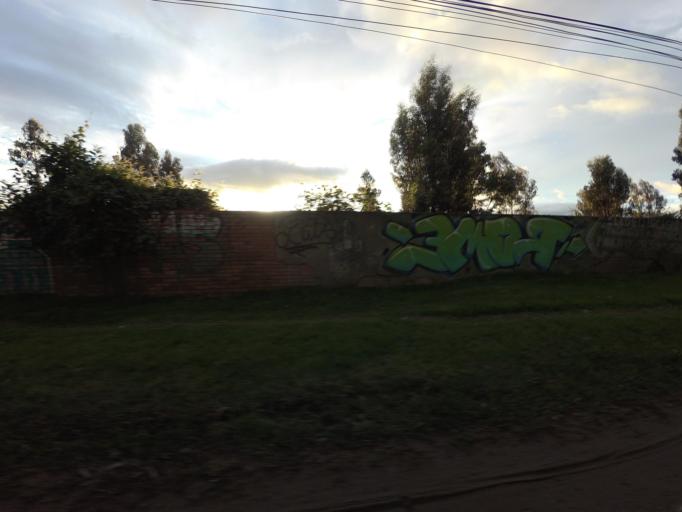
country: CO
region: Cundinamarca
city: La Calera
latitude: 4.7722
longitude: -74.0272
